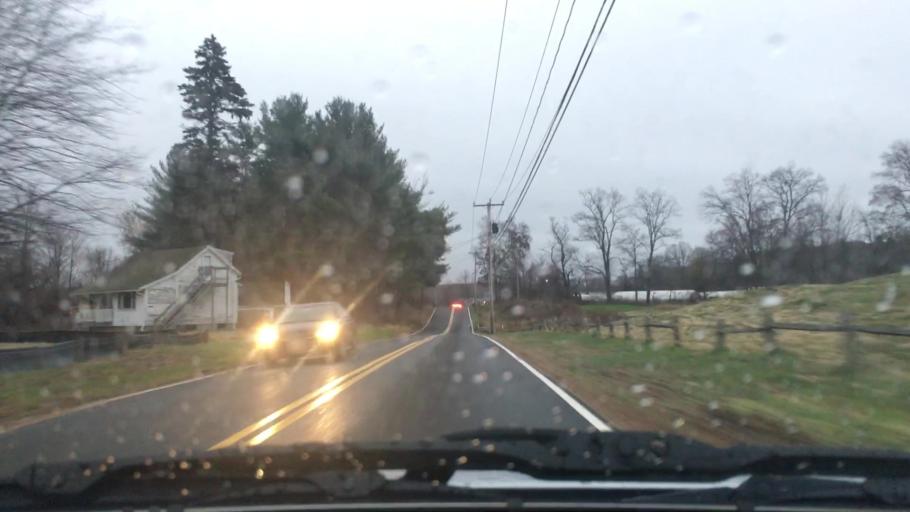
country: US
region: Massachusetts
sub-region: Hampden County
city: Southwick
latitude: 42.0803
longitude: -72.7703
